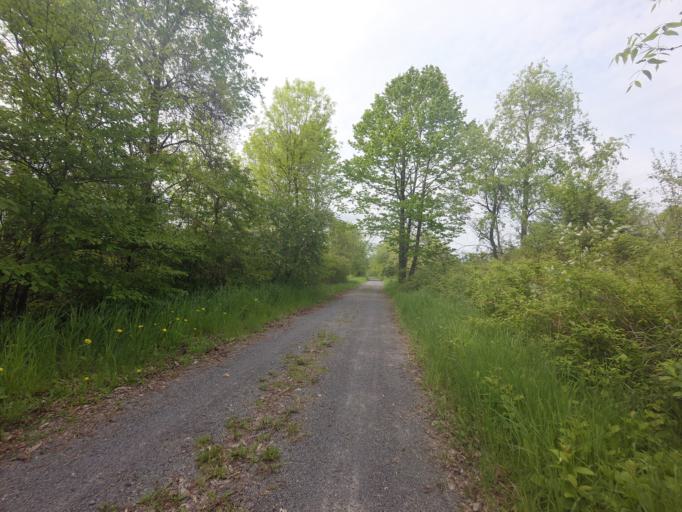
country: CA
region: Ontario
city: Kingston
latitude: 44.3661
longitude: -76.6270
